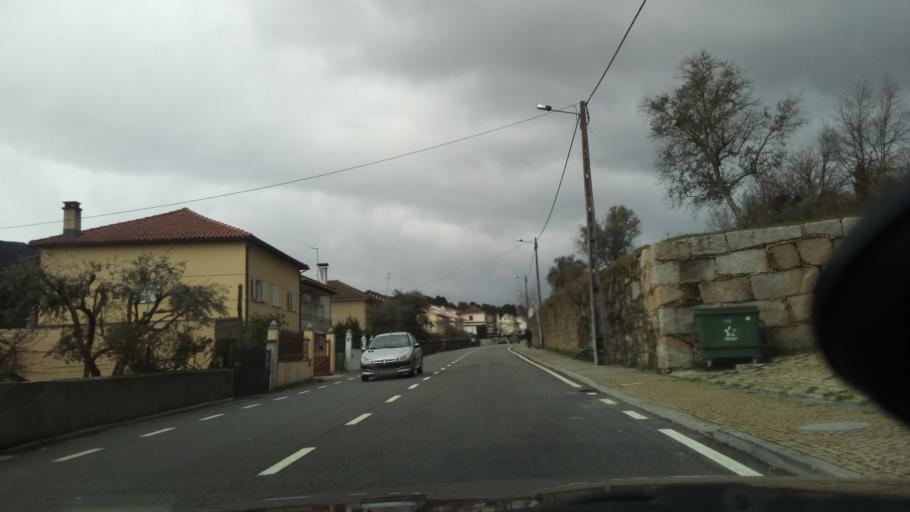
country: PT
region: Guarda
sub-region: Fornos de Algodres
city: Fornos de Algodres
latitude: 40.5153
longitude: -7.5826
